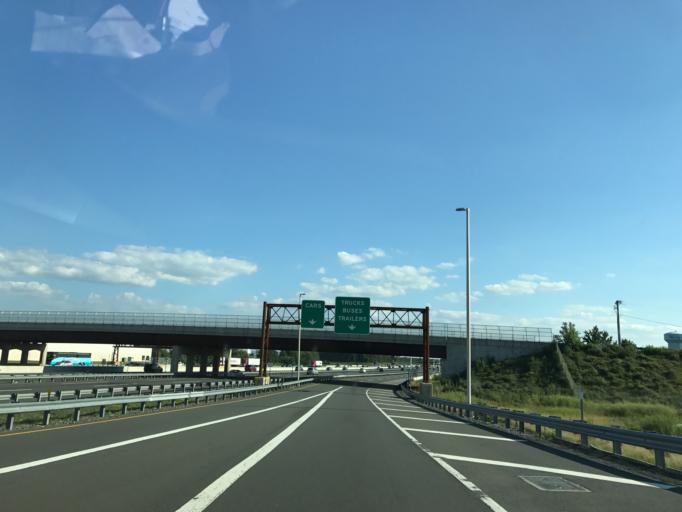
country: US
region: New Jersey
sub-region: Middlesex County
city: Rossmoor
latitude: 40.3281
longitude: -74.4845
